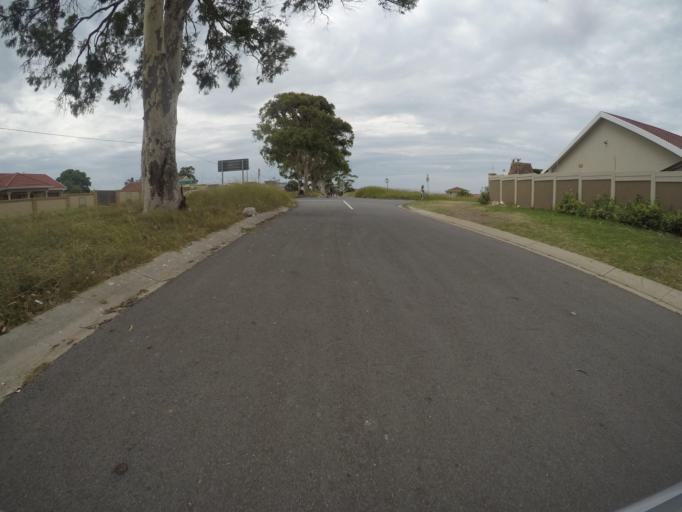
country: ZA
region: Eastern Cape
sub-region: Buffalo City Metropolitan Municipality
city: East London
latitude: -32.9995
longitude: 27.8747
